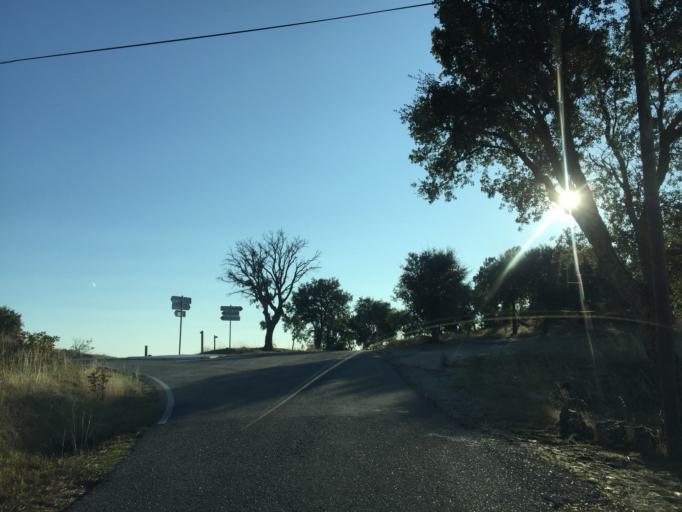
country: PT
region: Portalegre
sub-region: Castelo de Vide
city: Castelo de Vide
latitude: 39.4000
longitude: -7.4491
